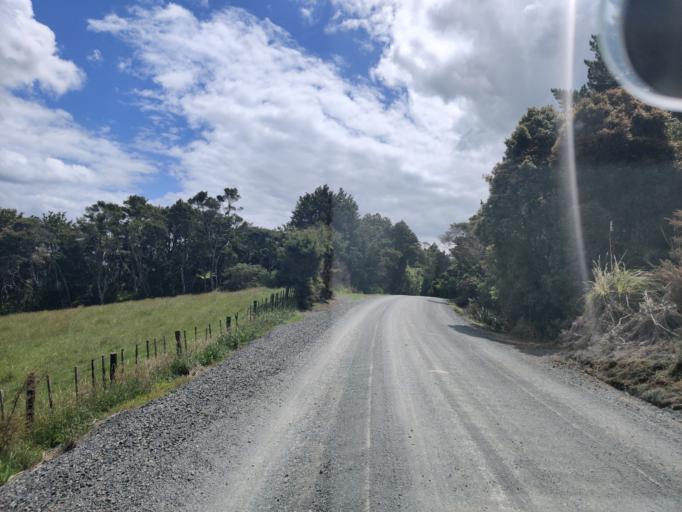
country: NZ
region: Northland
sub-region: Far North District
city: Paihia
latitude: -35.2595
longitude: 174.0618
